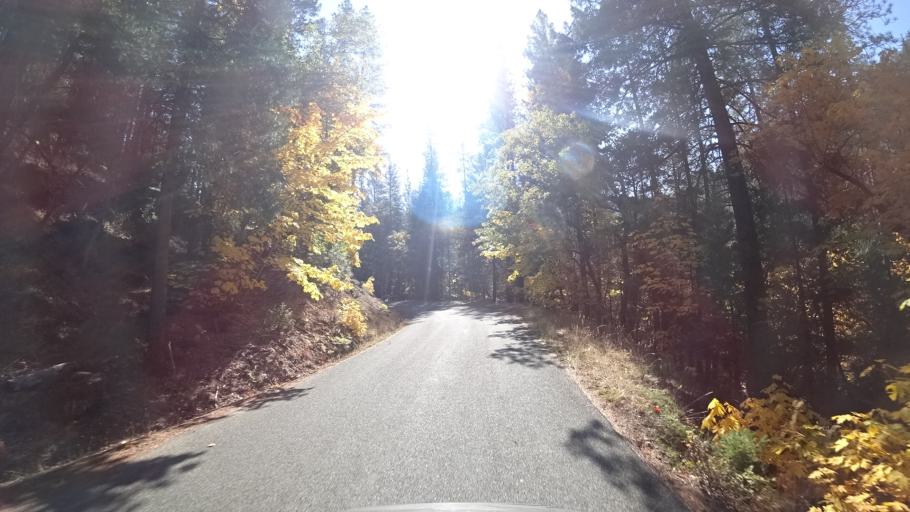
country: US
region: California
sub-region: Siskiyou County
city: Happy Camp
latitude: 41.6368
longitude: -123.1064
